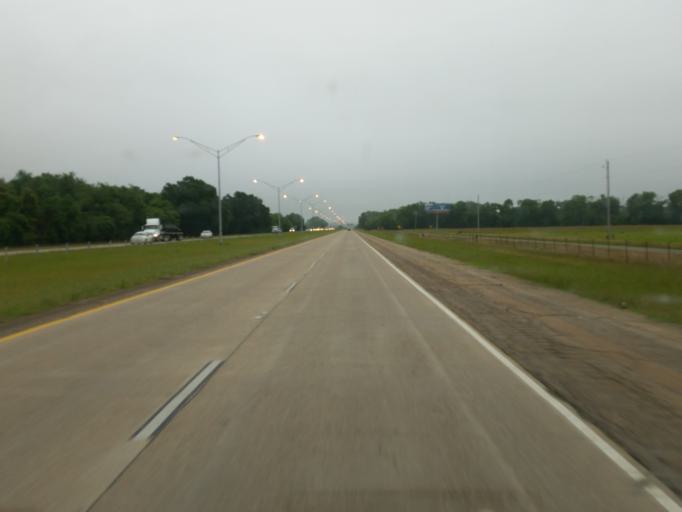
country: US
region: Louisiana
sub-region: Bossier Parish
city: Red Chute
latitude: 32.5341
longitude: -93.6518
